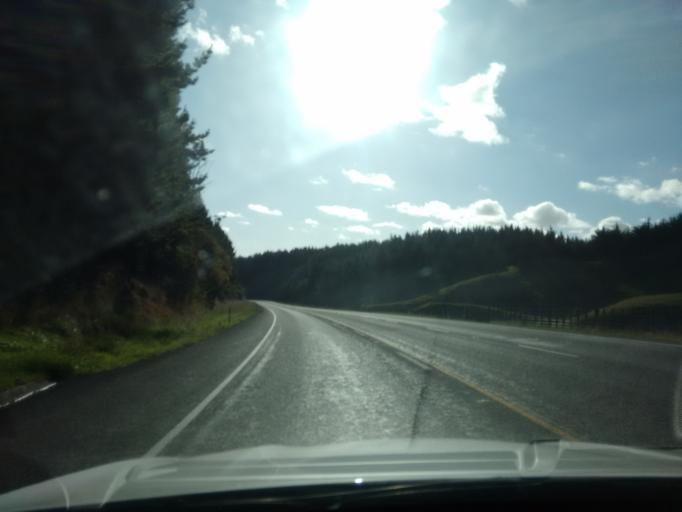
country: NZ
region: Manawatu-Wanganui
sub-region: Wanganui District
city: Wanganui
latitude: -39.8336
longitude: 174.9073
